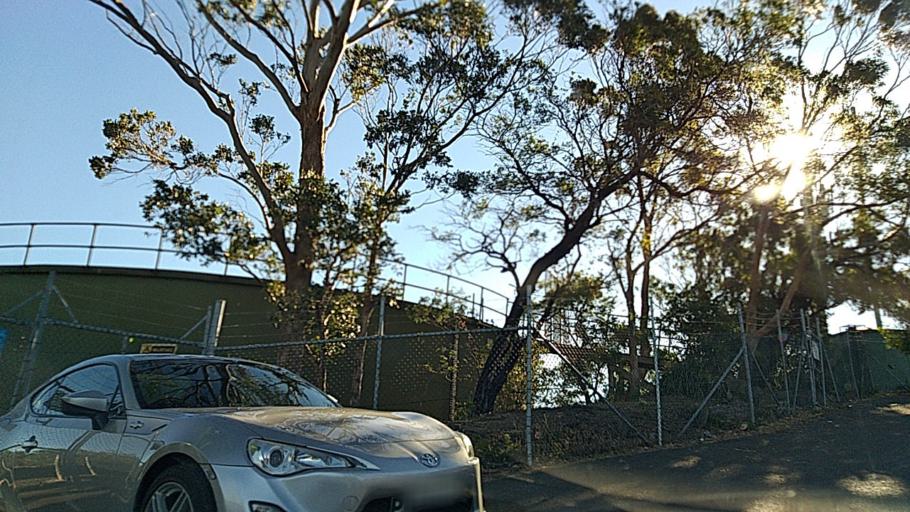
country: AU
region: New South Wales
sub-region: Wollongong
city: Mount Keira
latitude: -34.4223
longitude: 150.8403
